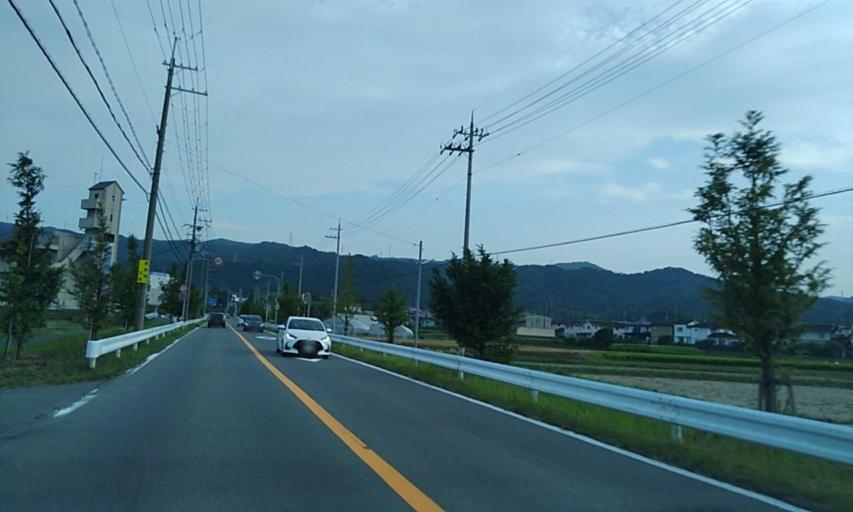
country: JP
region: Kyoto
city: Kameoka
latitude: 34.9987
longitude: 135.6041
